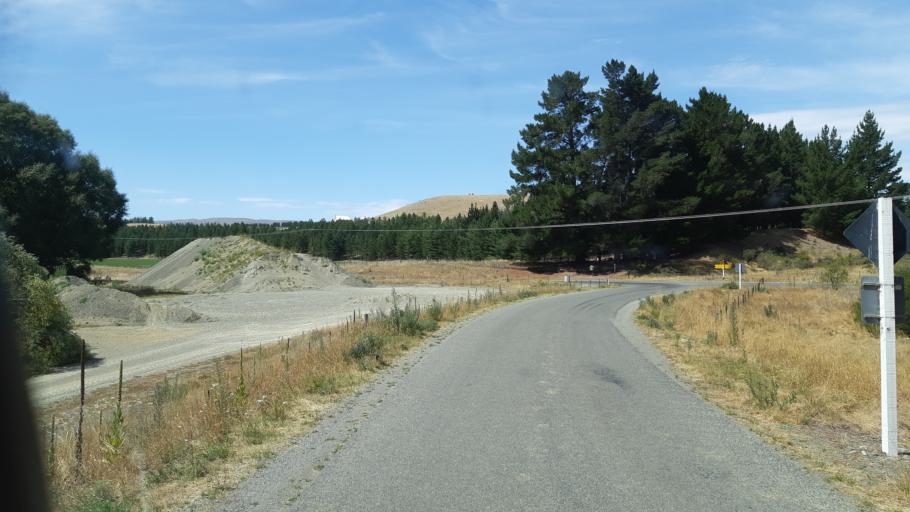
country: NZ
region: Otago
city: Oamaru
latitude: -44.6606
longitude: 170.6020
